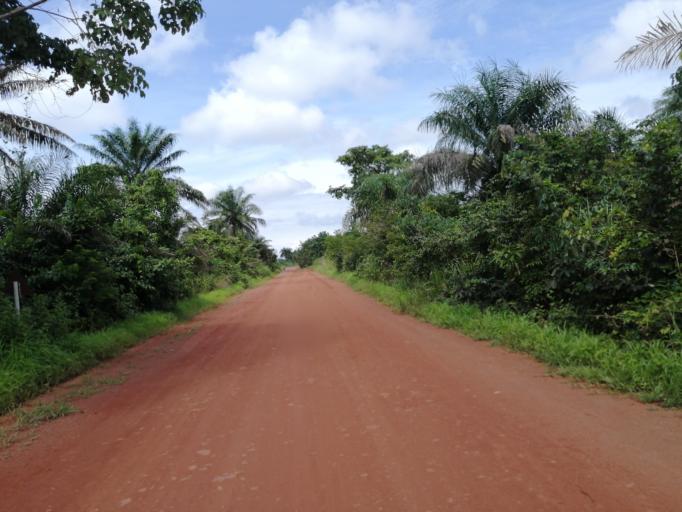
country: SL
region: Northern Province
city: Pepel
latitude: 8.6628
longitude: -13.0030
